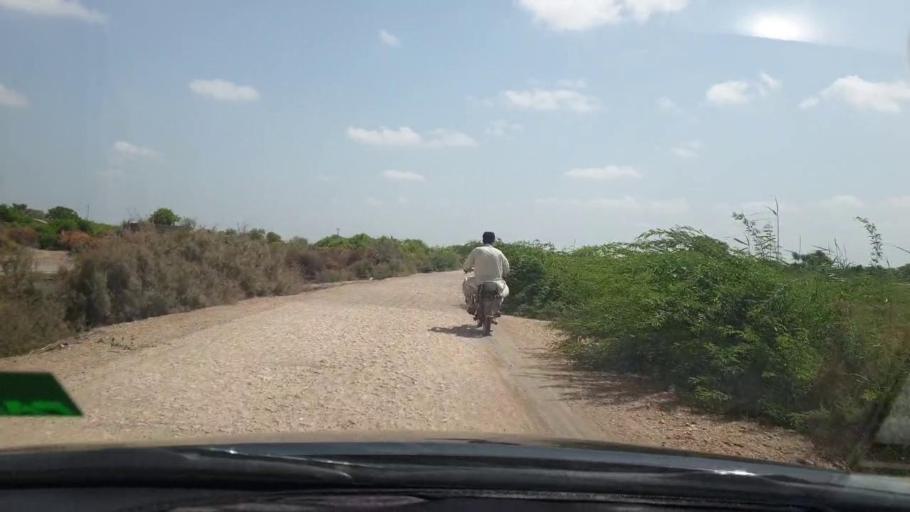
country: PK
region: Sindh
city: Tando Bago
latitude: 24.8786
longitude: 69.0812
